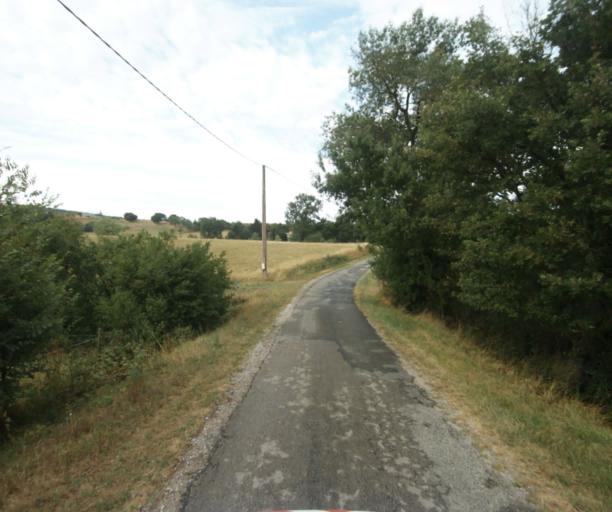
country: FR
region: Midi-Pyrenees
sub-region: Departement de la Haute-Garonne
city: Revel
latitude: 43.4268
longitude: 1.9912
